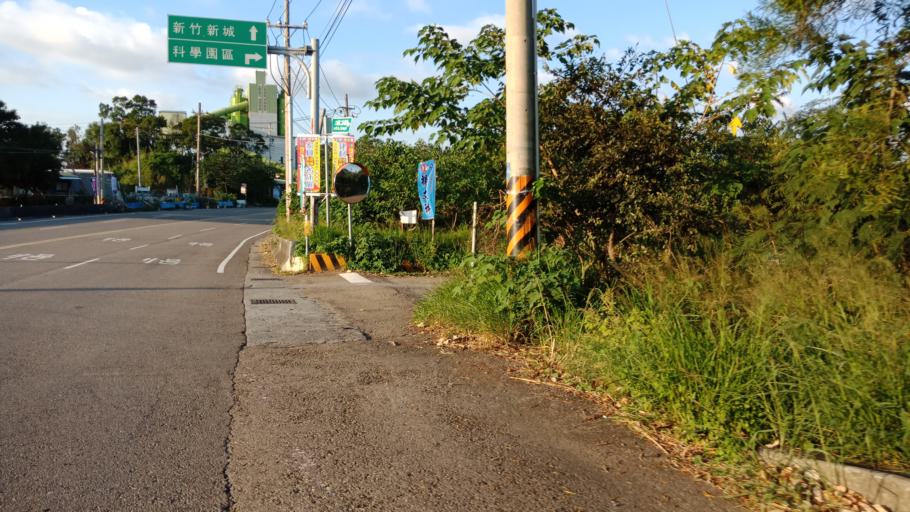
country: TW
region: Taiwan
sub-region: Hsinchu
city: Hsinchu
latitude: 24.7570
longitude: 120.9990
